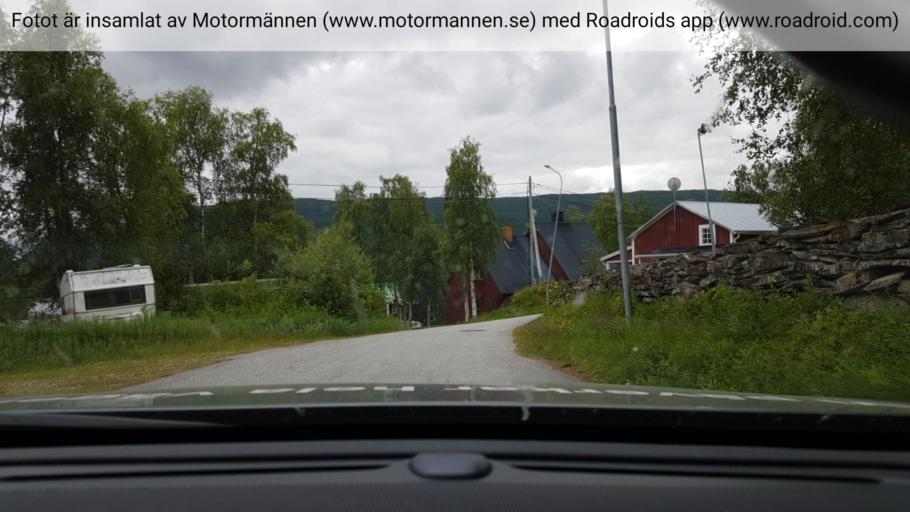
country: SE
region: Vaesterbotten
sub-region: Storumans Kommun
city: Fristad
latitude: 65.9607
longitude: 16.2194
